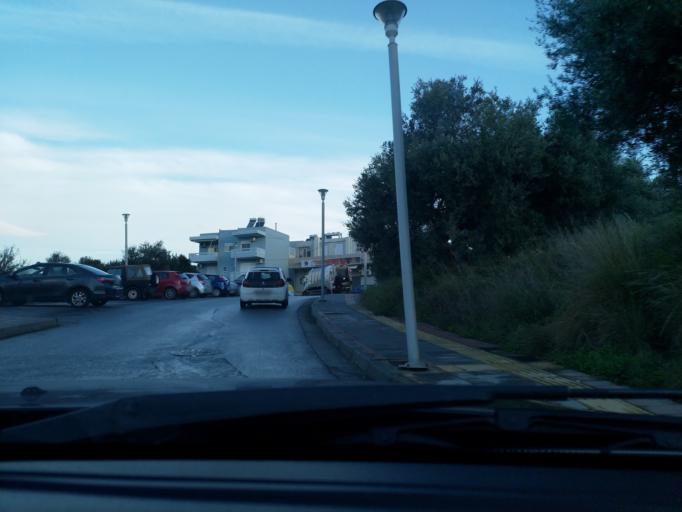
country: GR
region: Crete
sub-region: Nomos Chanias
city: Chania
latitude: 35.5125
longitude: 24.0474
